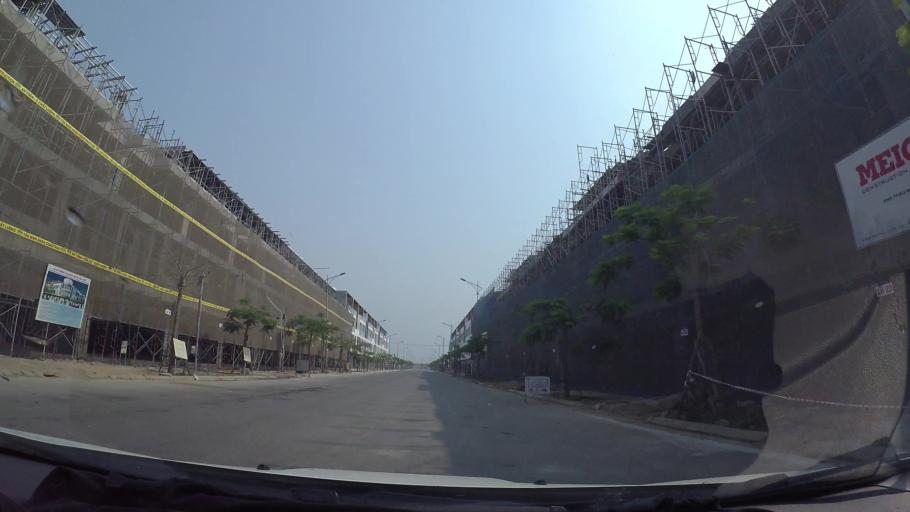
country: VN
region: Da Nang
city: Ngu Hanh Son
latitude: 16.0057
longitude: 108.2394
